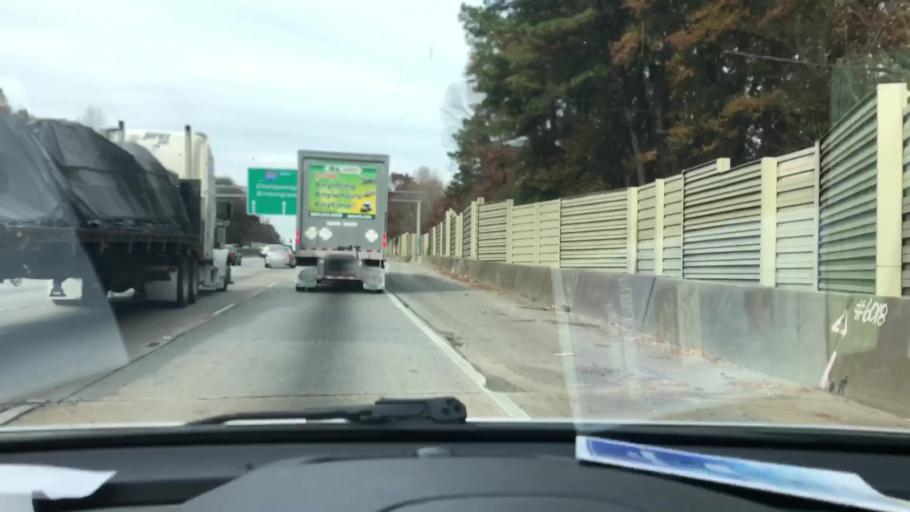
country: US
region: Georgia
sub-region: DeKalb County
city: Tucker
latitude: 33.8724
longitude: -84.2496
